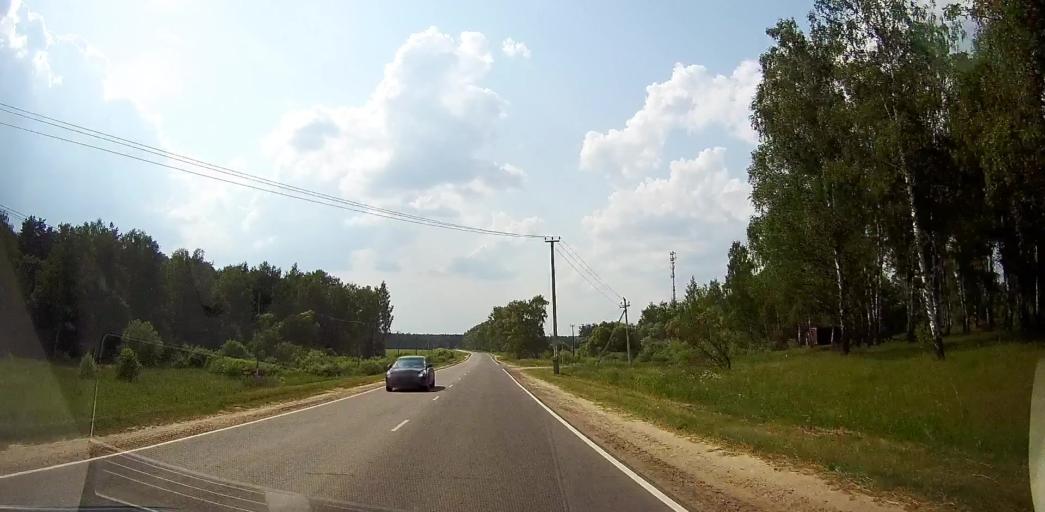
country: RU
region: Moskovskaya
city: Zhilevo
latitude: 55.0566
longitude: 37.9693
